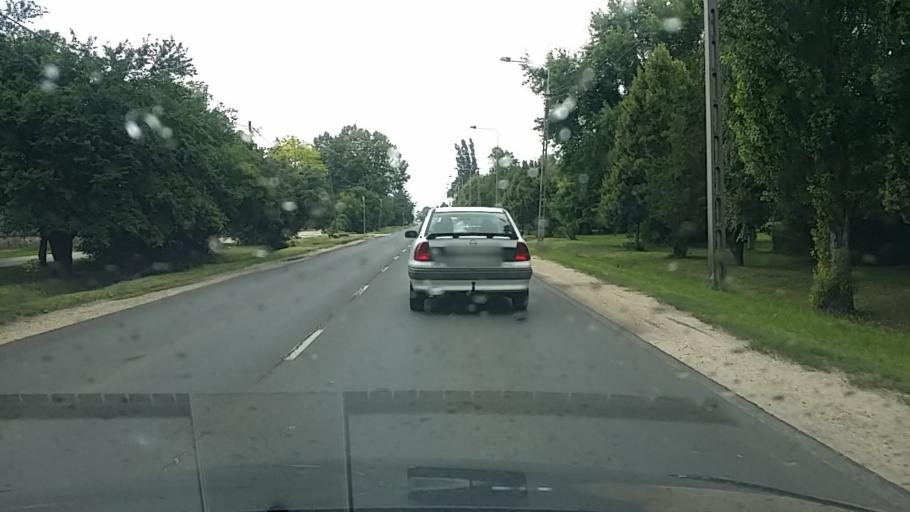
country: HU
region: Pest
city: Orkeny
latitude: 47.1287
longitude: 19.4256
